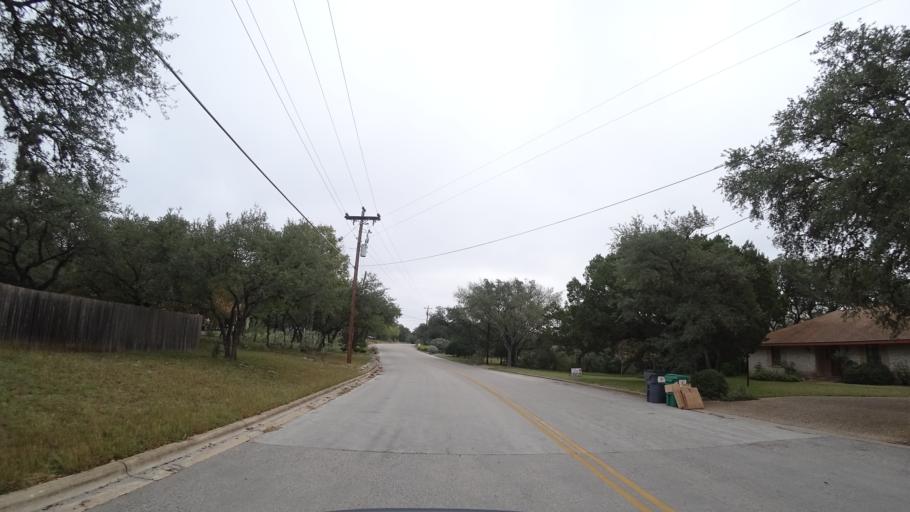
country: US
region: Texas
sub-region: Travis County
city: Shady Hollow
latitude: 30.2194
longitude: -97.9075
